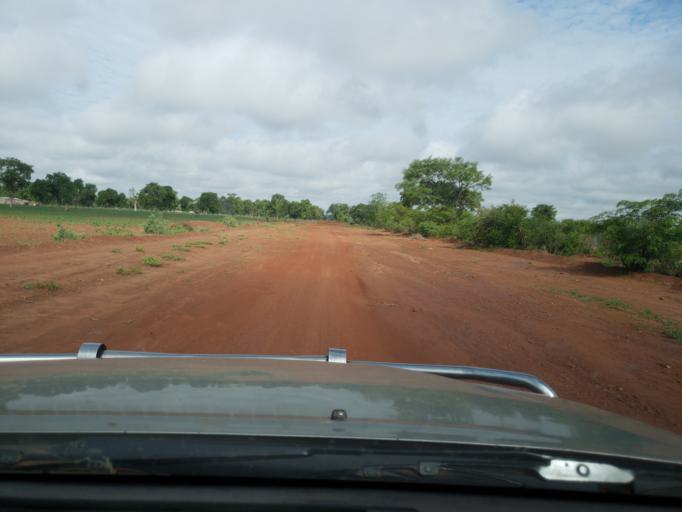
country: ML
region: Sikasso
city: Koutiala
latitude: 12.3924
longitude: -6.0078
